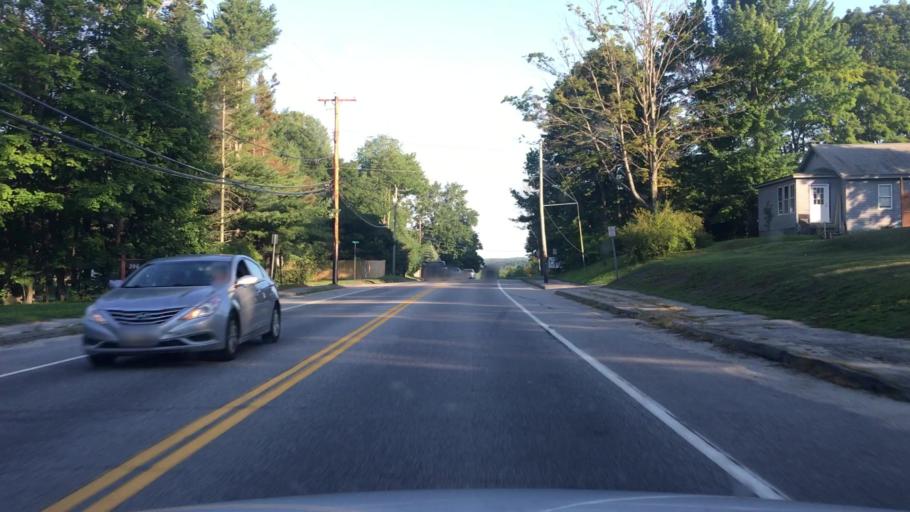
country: US
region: Maine
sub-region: Androscoggin County
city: Lisbon
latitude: 44.0172
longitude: -70.0916
